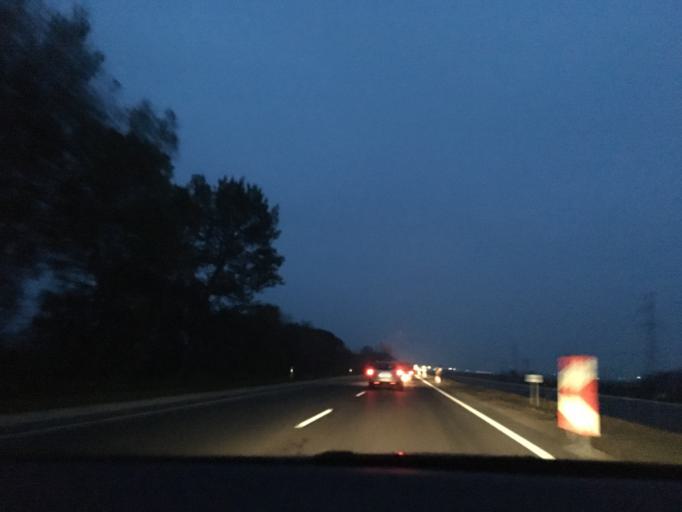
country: HU
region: Pest
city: Cegled
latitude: 47.2114
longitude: 19.7451
